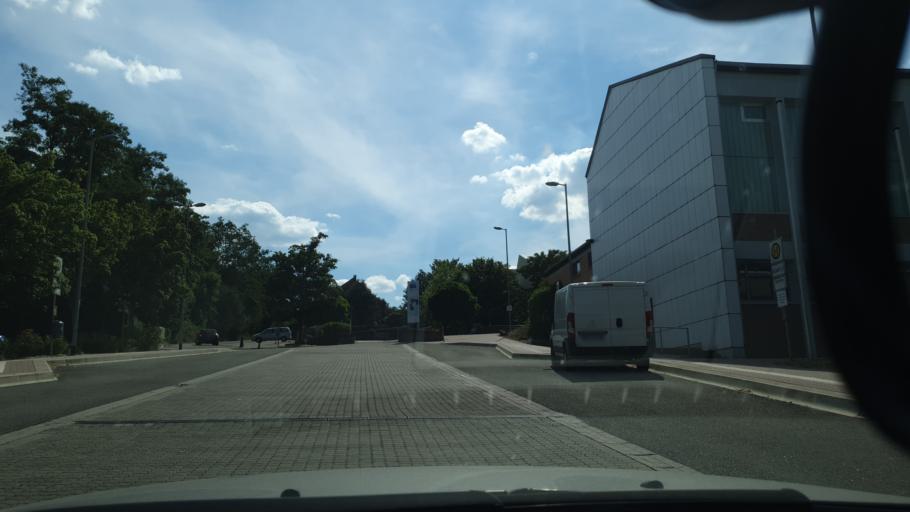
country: DE
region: Rheinland-Pfalz
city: Otterberg
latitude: 49.5003
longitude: 7.7648
